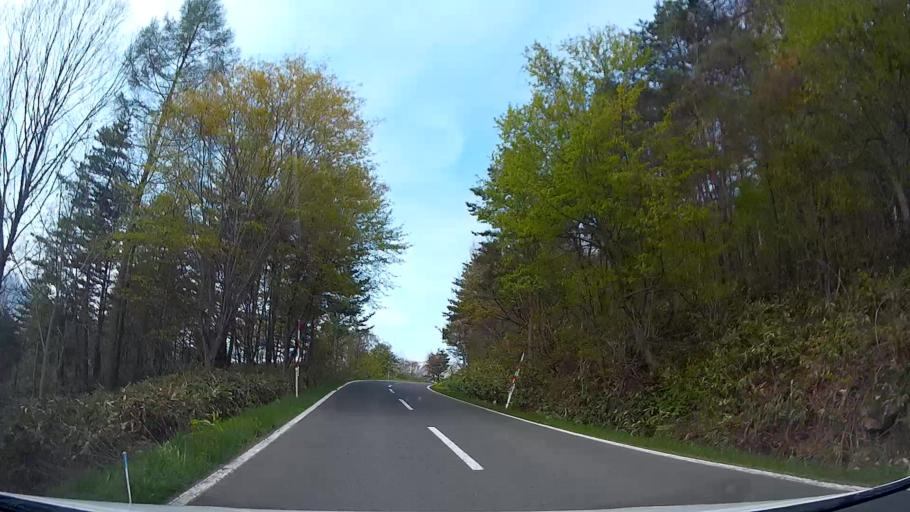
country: JP
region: Iwate
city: Shizukuishi
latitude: 39.9252
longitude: 140.9729
